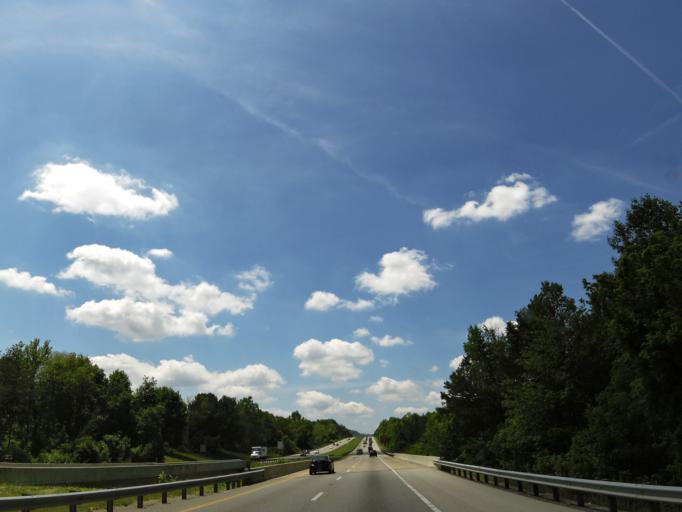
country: US
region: Kentucky
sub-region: Whitley County
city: Corbin
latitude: 36.9365
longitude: -84.1253
